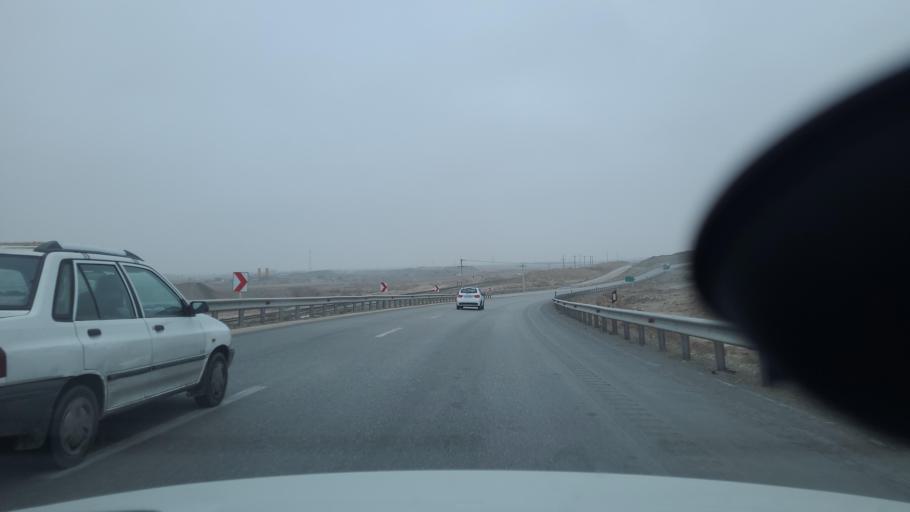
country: IR
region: Razavi Khorasan
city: Fariman
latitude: 35.9979
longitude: 59.7591
